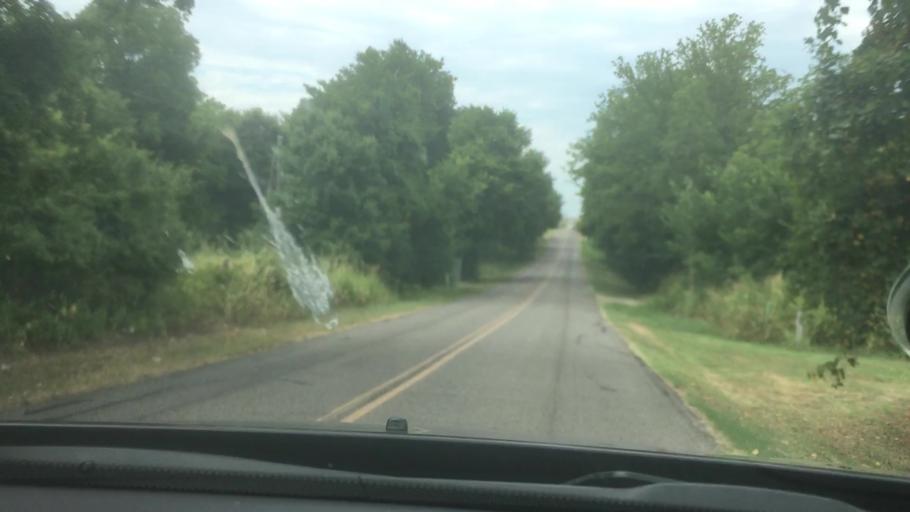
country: US
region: Oklahoma
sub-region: Murray County
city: Davis
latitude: 34.4952
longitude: -97.0554
